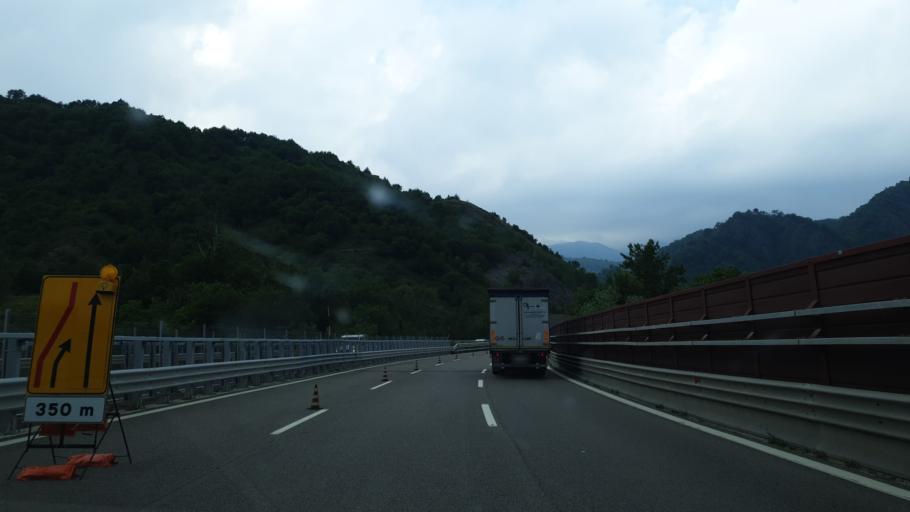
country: IT
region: Veneto
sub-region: Provincia di Treviso
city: Carpesica
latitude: 45.9735
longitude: 12.2835
